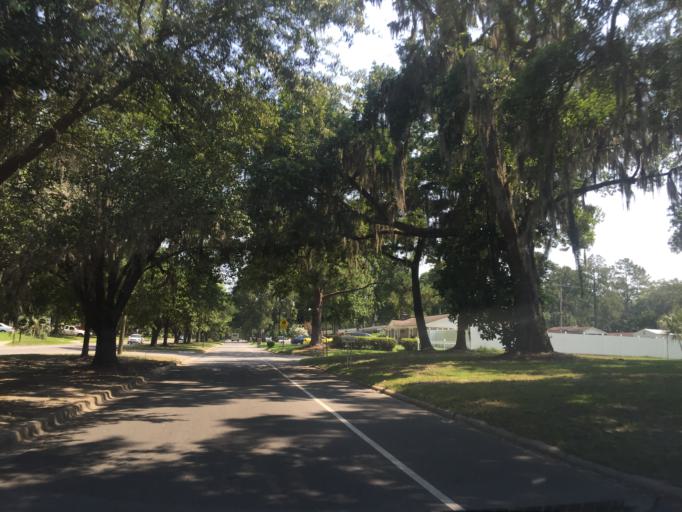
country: US
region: Georgia
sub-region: Chatham County
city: Montgomery
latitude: 31.9750
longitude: -81.1509
